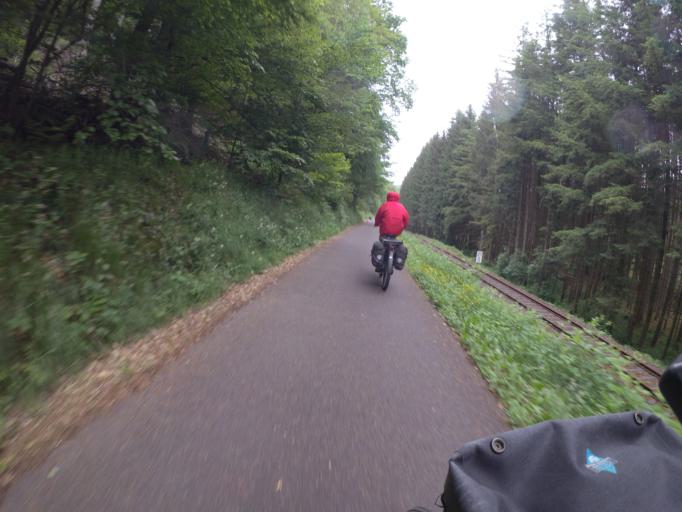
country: DE
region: Rheinland-Pfalz
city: Steinalben
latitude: 49.3038
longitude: 7.6602
